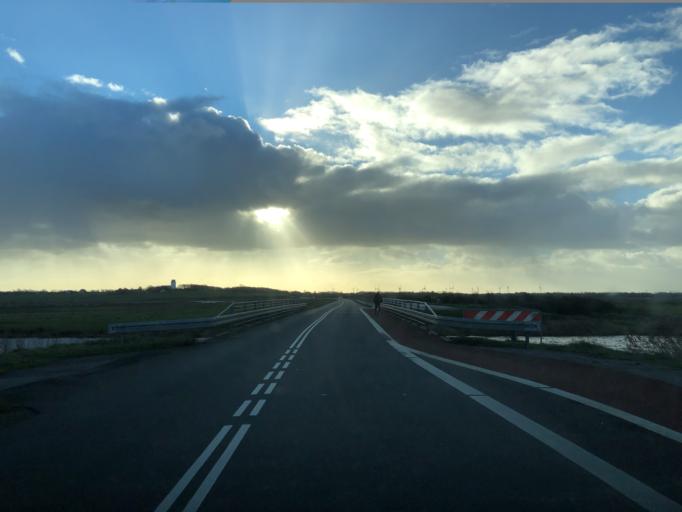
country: DK
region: Central Jutland
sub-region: Ringkobing-Skjern Kommune
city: Skjern
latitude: 55.9151
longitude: 8.4374
